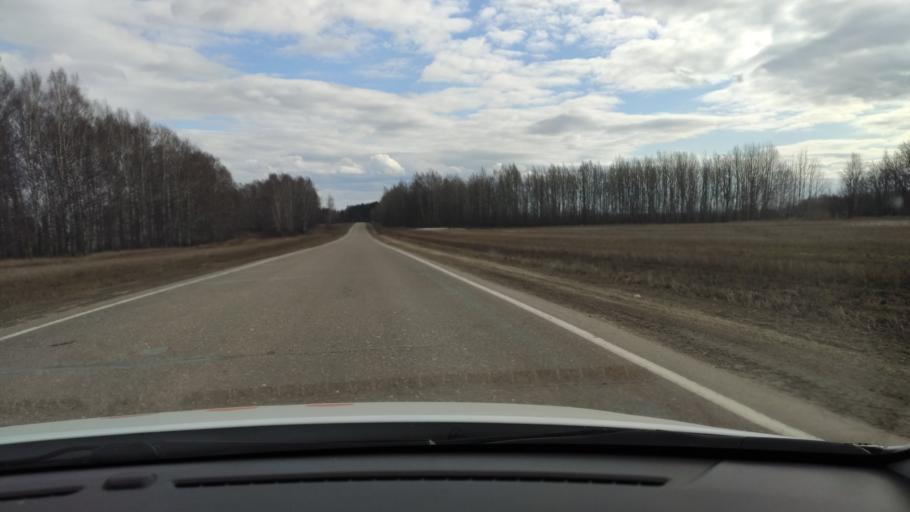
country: RU
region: Tatarstan
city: Vysokaya Gora
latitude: 56.0728
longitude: 49.1913
